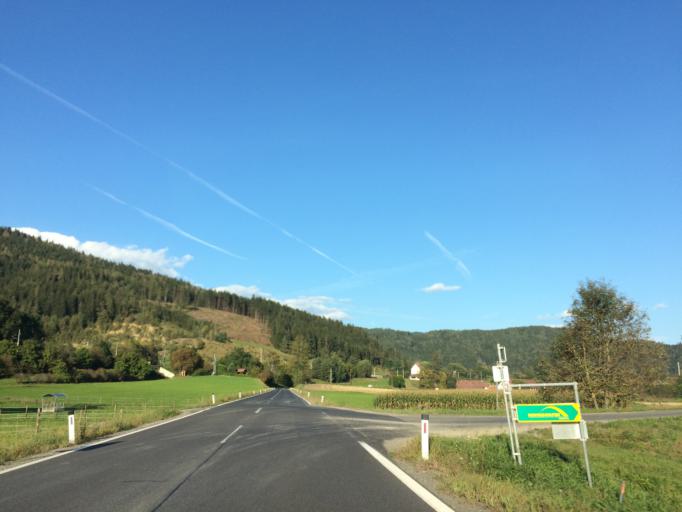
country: AT
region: Styria
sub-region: Politischer Bezirk Leoben
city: Sankt Michael in Obersteiermark
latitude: 47.3372
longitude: 14.9955
